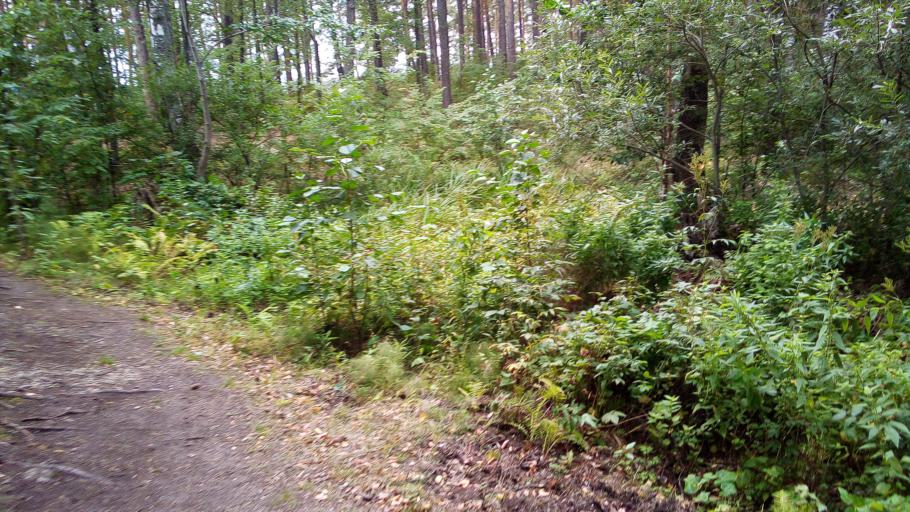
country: RU
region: Chelyabinsk
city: Turgoyak
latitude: 55.1780
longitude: 60.0295
